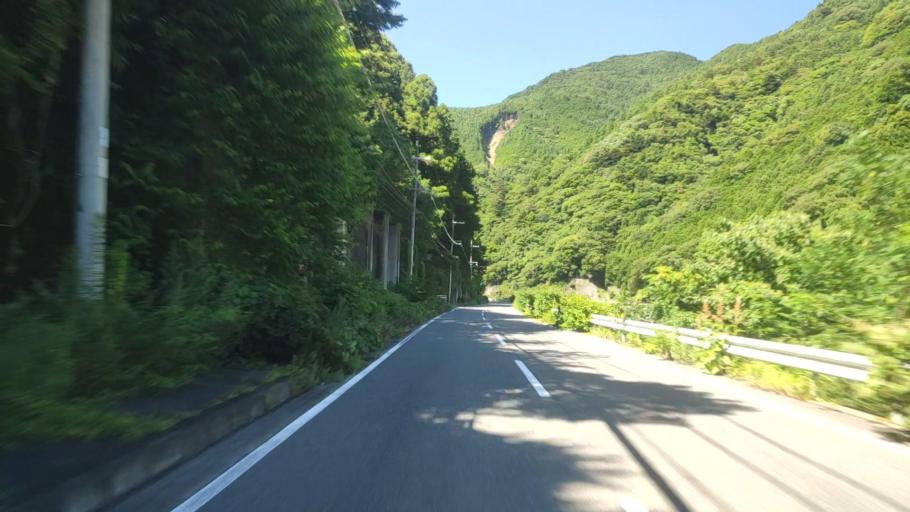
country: JP
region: Nara
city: Yoshino-cho
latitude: 34.3148
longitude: 135.9774
